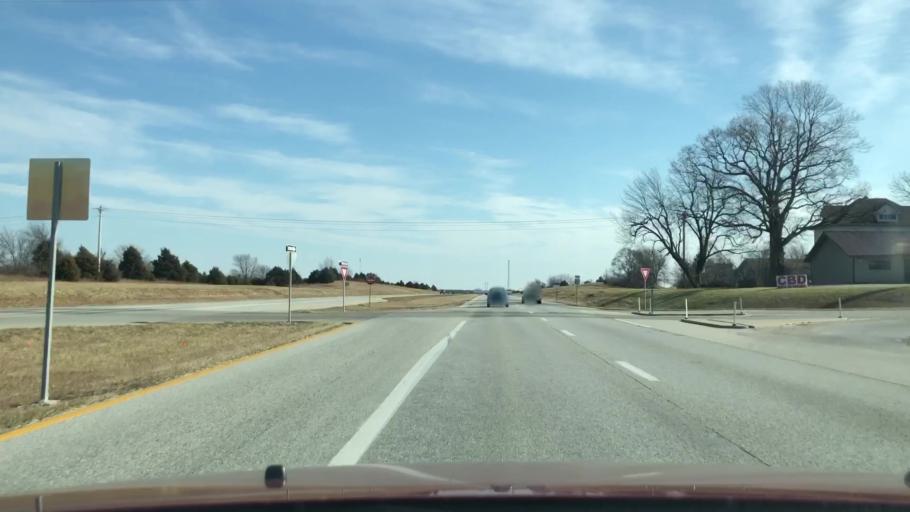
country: US
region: Missouri
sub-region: Webster County
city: Seymour
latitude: 37.1563
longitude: -92.7730
